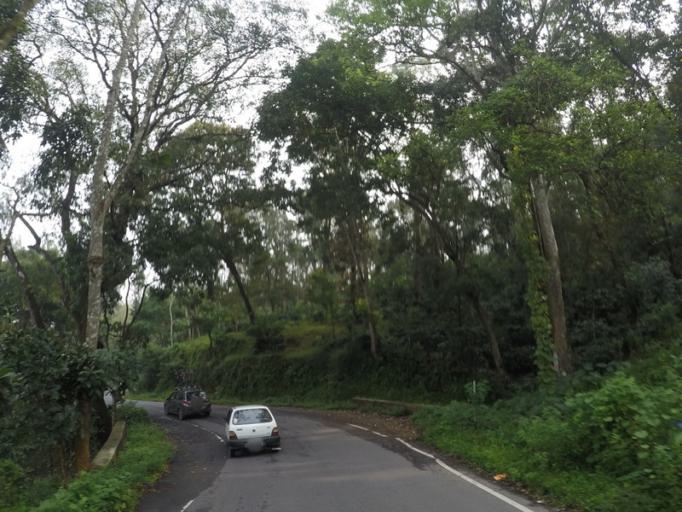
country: IN
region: Karnataka
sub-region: Chikmagalur
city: Mudigere
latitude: 13.2644
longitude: 75.6249
